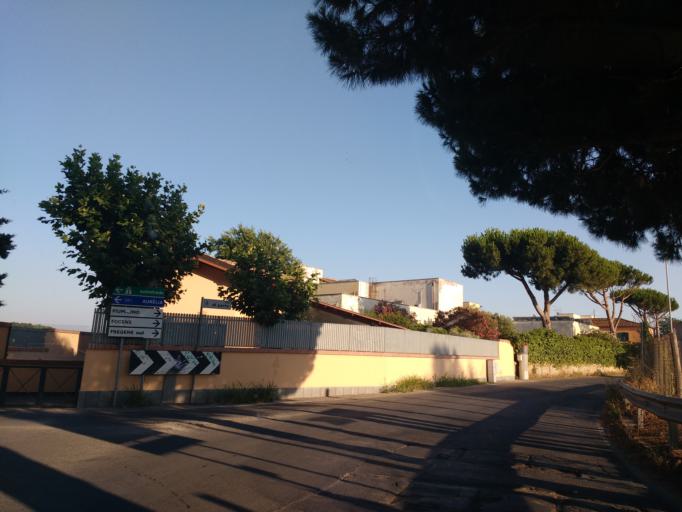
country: IT
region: Latium
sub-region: Citta metropolitana di Roma Capitale
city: Fregene
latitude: 41.8543
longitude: 12.2185
